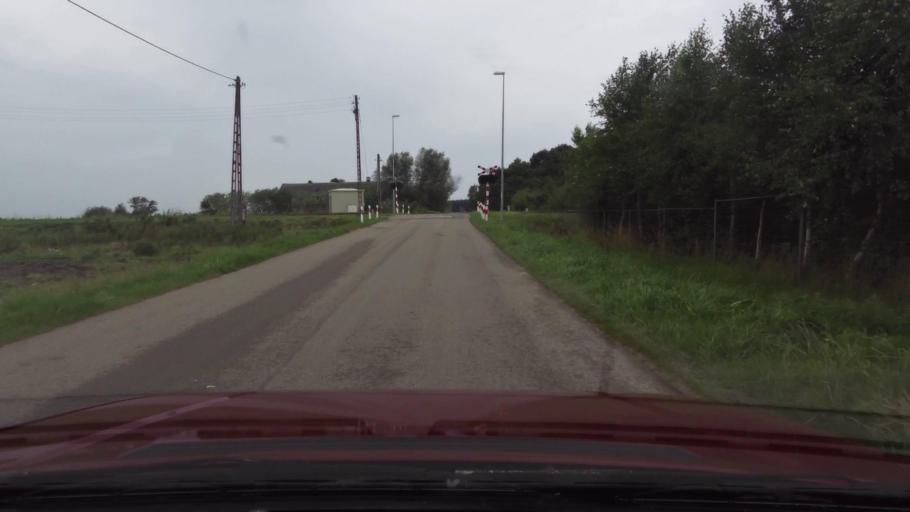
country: PL
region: West Pomeranian Voivodeship
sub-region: Powiat kolobrzeski
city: Grzybowo
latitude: 54.1459
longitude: 15.5102
